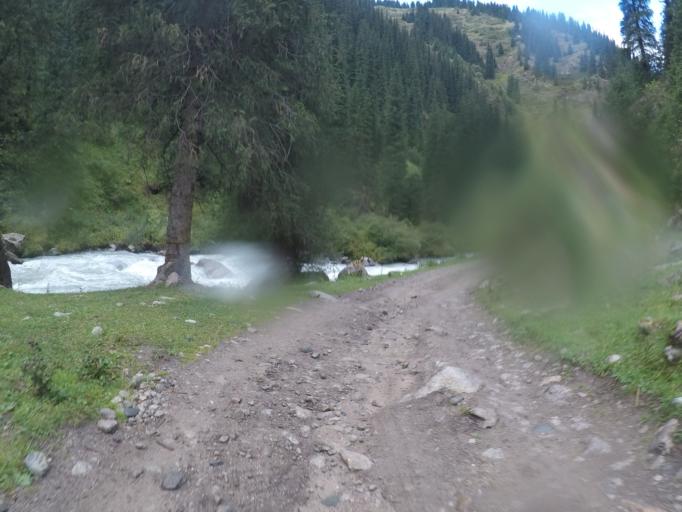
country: KG
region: Ysyk-Koel
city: Teploklyuchenka
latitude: 42.4140
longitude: 78.5725
